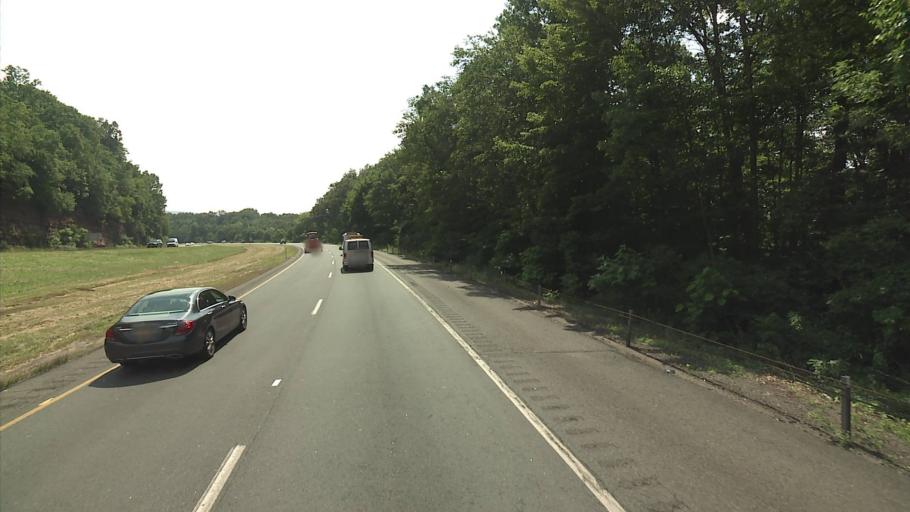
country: US
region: Connecticut
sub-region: New Haven County
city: Meriden
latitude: 41.5484
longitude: -72.8268
